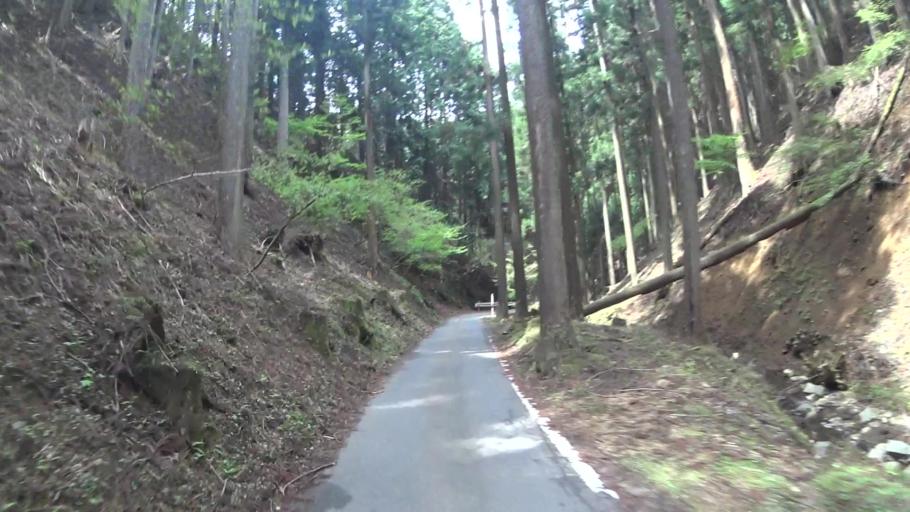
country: JP
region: Kyoto
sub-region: Kyoto-shi
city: Kamigyo-ku
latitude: 35.1560
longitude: 135.7524
